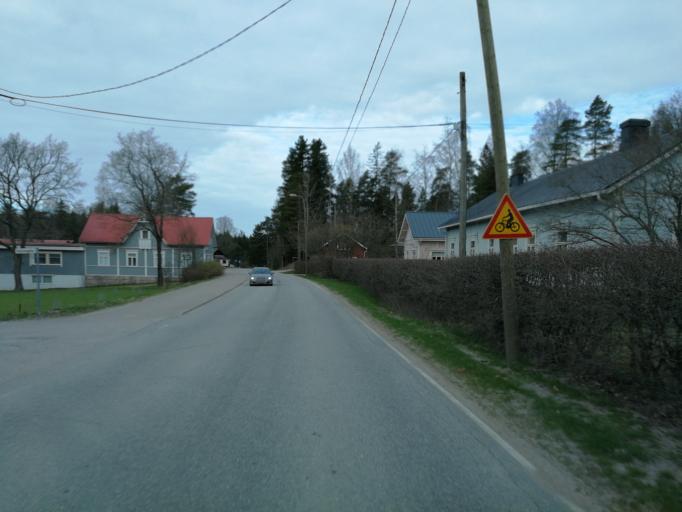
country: FI
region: Varsinais-Suomi
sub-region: Salo
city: Muurla
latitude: 60.3493
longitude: 23.2728
